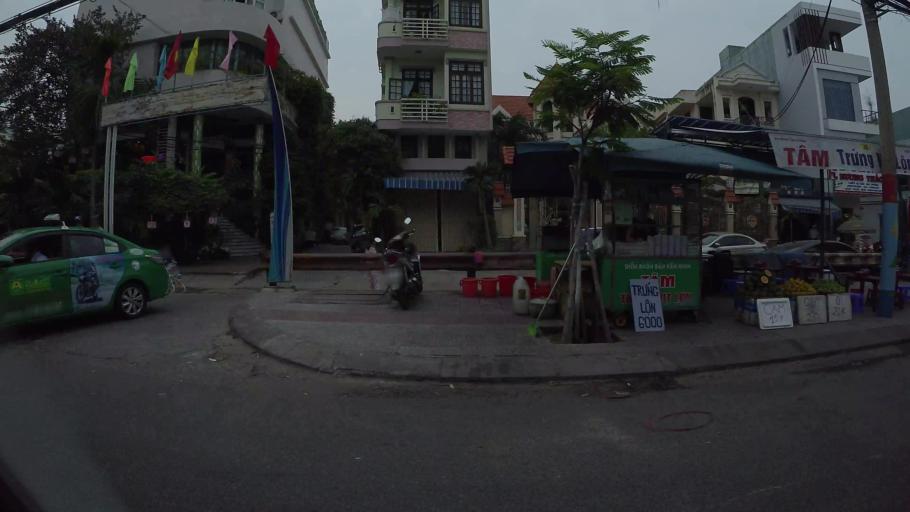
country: VN
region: Da Nang
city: Thanh Khe
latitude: 16.0693
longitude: 108.2052
